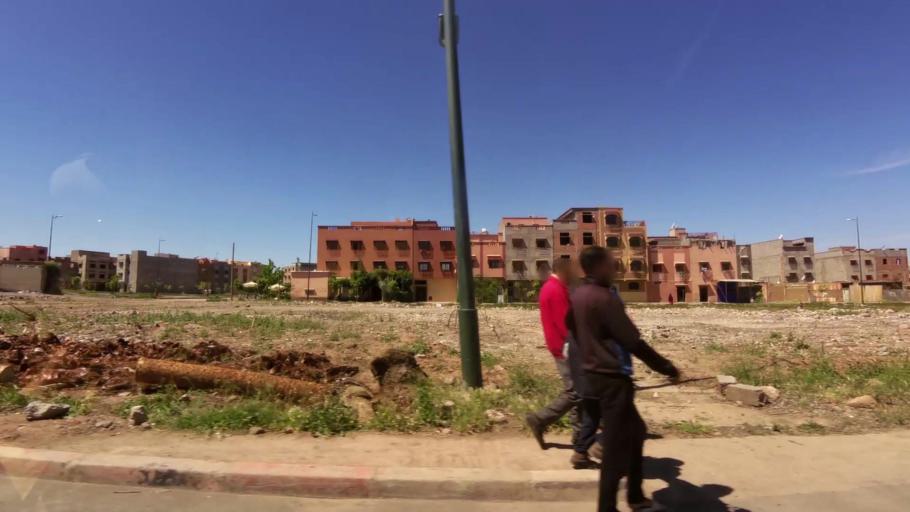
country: MA
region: Marrakech-Tensift-Al Haouz
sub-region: Marrakech
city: Marrakesh
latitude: 31.5602
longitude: -7.9779
